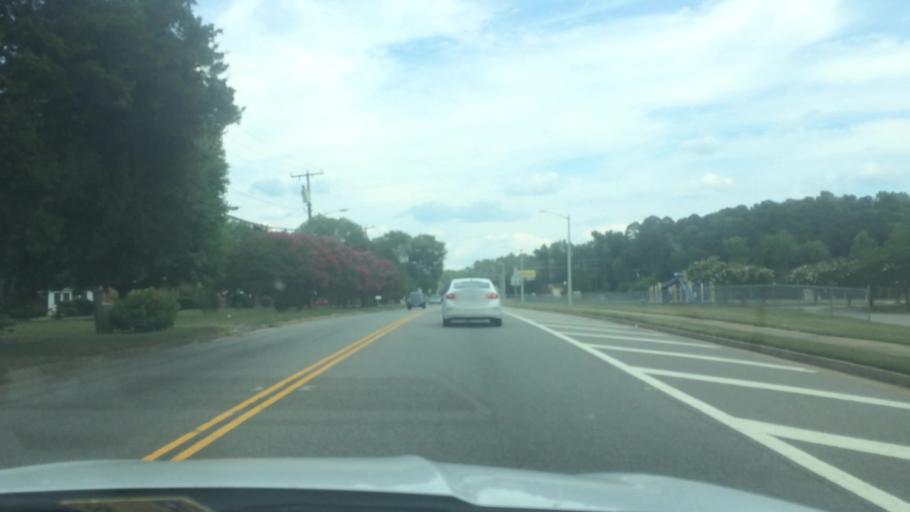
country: US
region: Virginia
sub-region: York County
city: Yorktown
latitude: 37.1889
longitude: -76.5717
